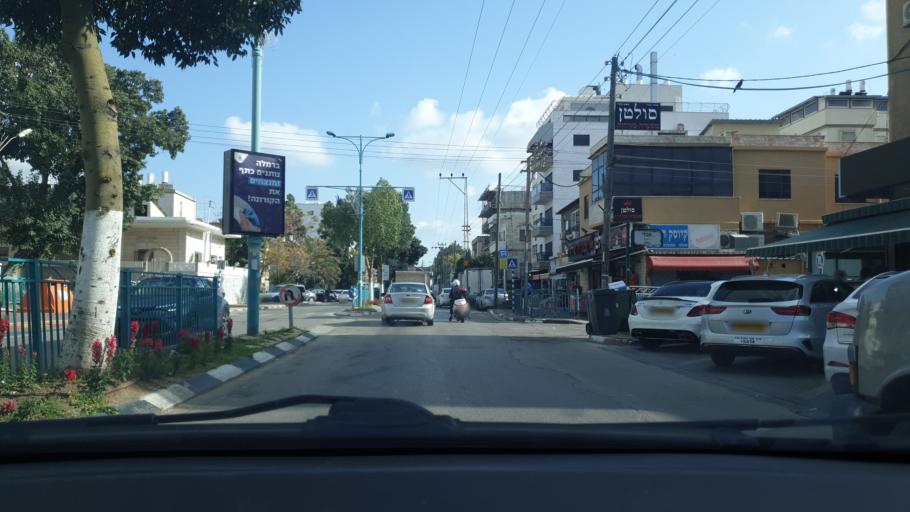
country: IL
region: Central District
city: Ramla
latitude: 31.9339
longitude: 34.8678
